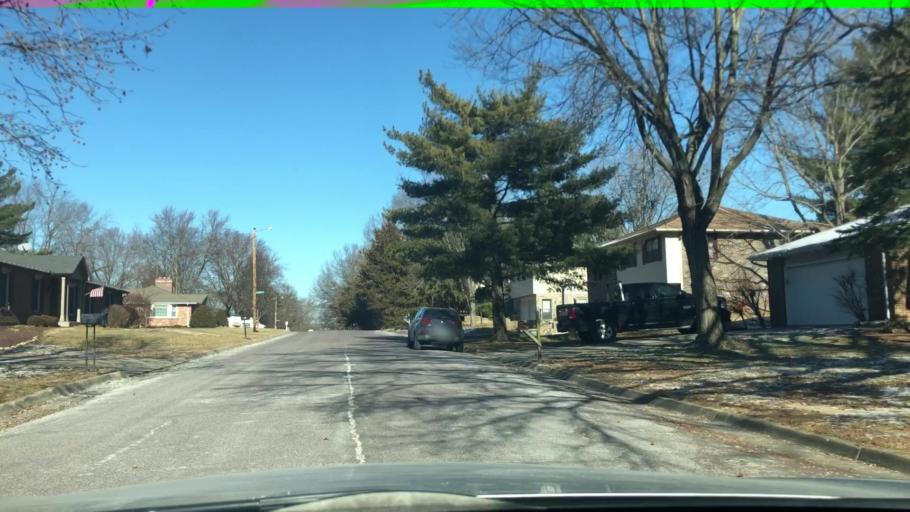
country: US
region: Missouri
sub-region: Boone County
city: Columbia
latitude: 38.9500
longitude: -92.3950
